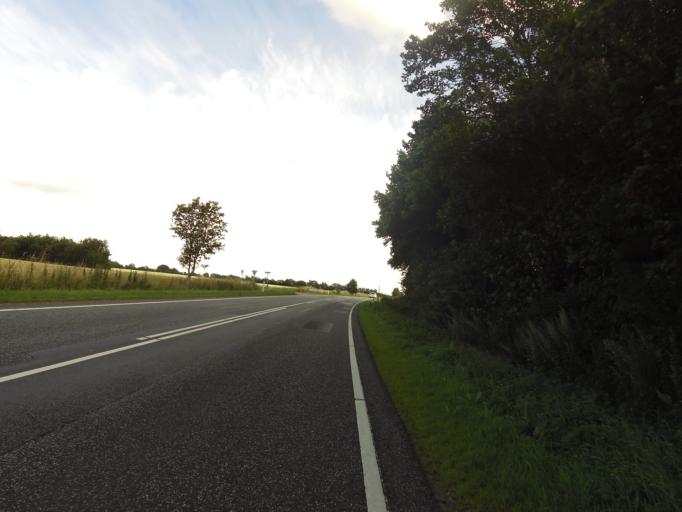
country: DK
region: South Denmark
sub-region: Tonder Kommune
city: Toftlund
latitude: 55.2130
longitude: 9.0387
